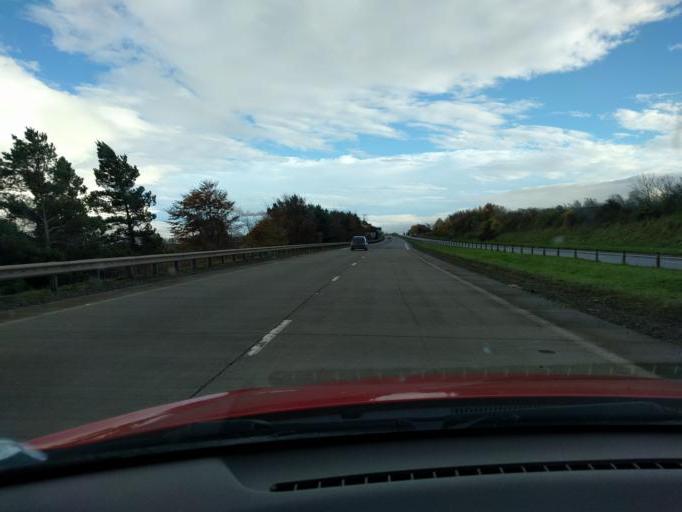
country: GB
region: Scotland
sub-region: East Lothian
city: Dunbar
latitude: 55.9853
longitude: -2.4957
